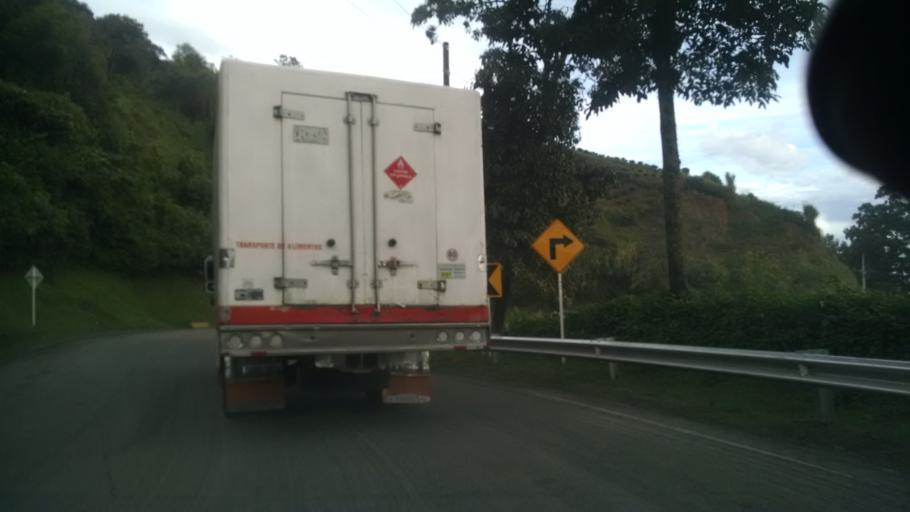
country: CO
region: Antioquia
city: Santa Barbara
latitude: 5.9102
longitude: -75.5753
